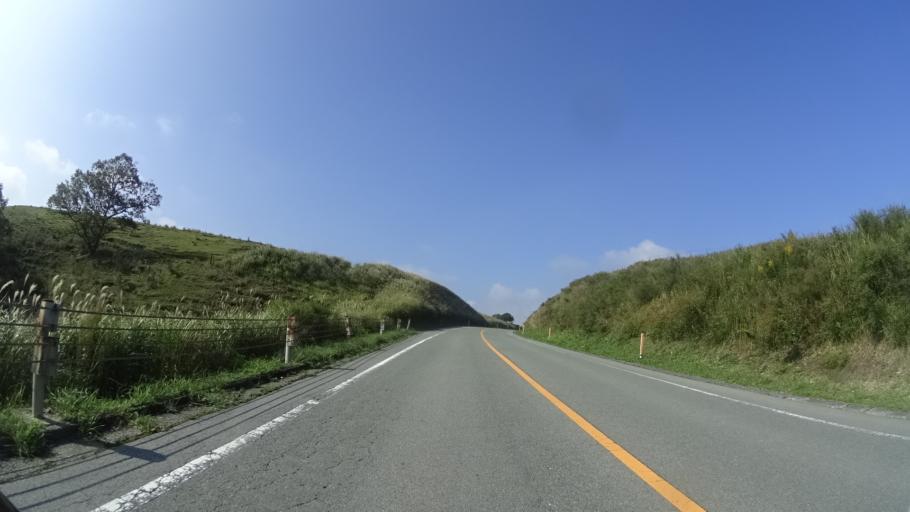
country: JP
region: Kumamoto
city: Aso
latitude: 33.0167
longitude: 131.0685
